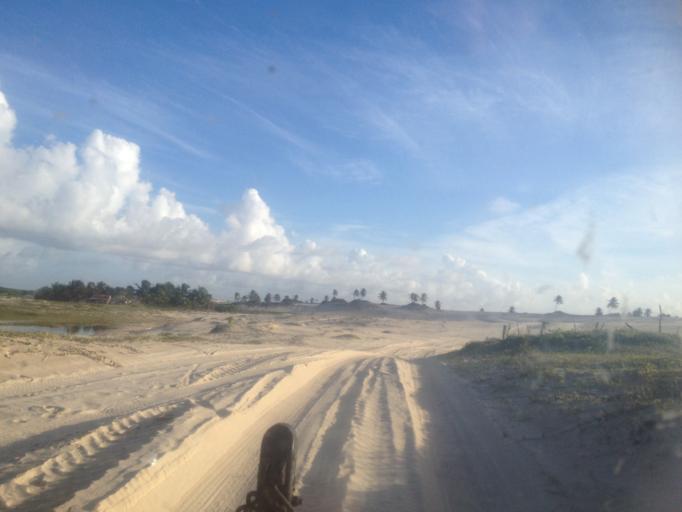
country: BR
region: Sergipe
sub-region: Indiaroba
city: Indiaroba
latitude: -11.4656
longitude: -37.3638
